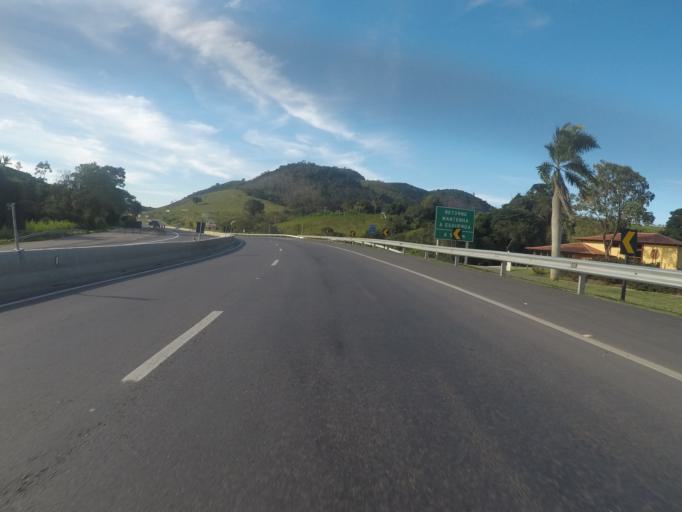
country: BR
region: Espirito Santo
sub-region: Ibiracu
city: Ibiracu
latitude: -19.8650
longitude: -40.3834
